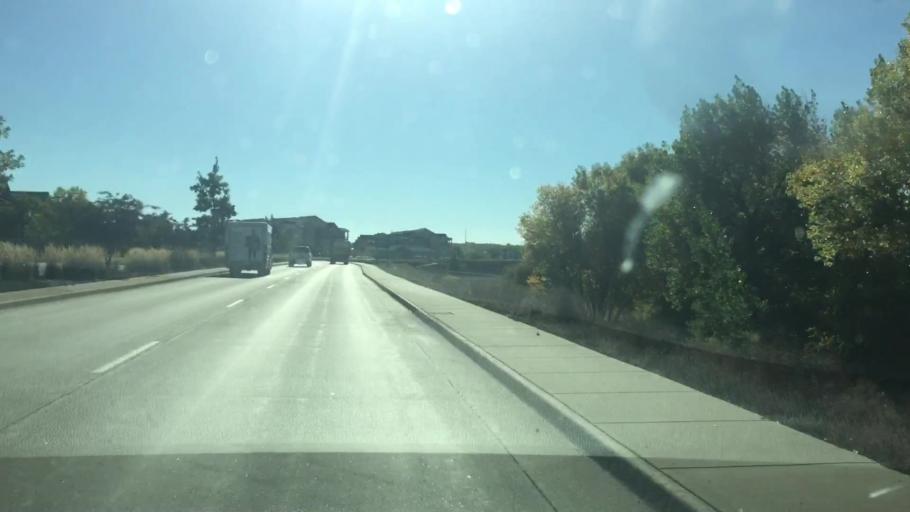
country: US
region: Colorado
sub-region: Douglas County
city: Parker
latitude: 39.5191
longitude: -104.7775
